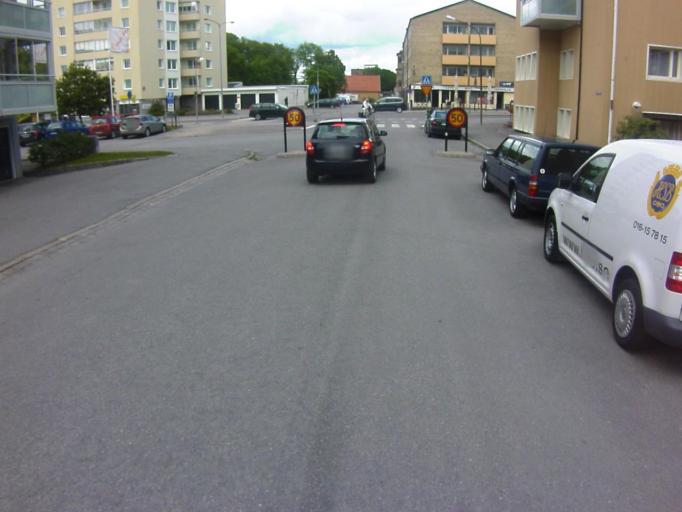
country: SE
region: Soedermanland
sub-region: Eskilstuna Kommun
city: Eskilstuna
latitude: 59.3605
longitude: 16.5135
